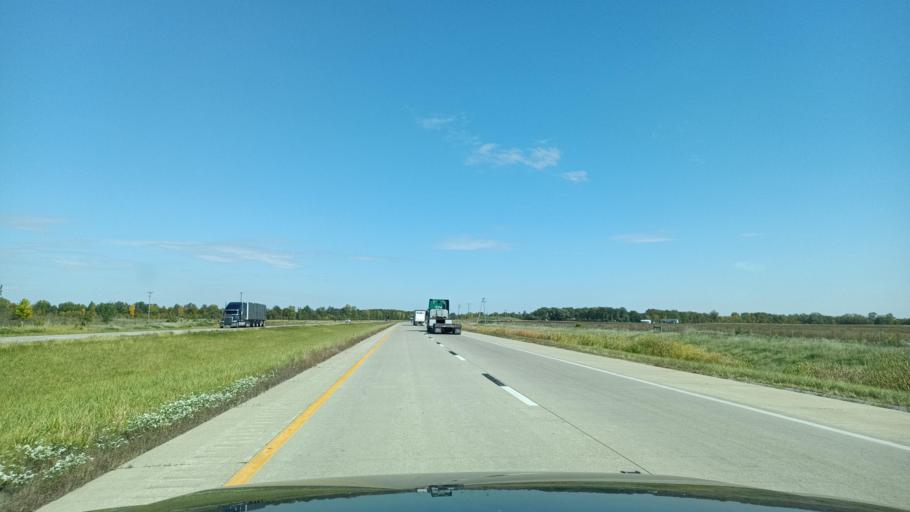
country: US
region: Ohio
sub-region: Paulding County
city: Antwerp
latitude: 41.1862
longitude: -84.6989
